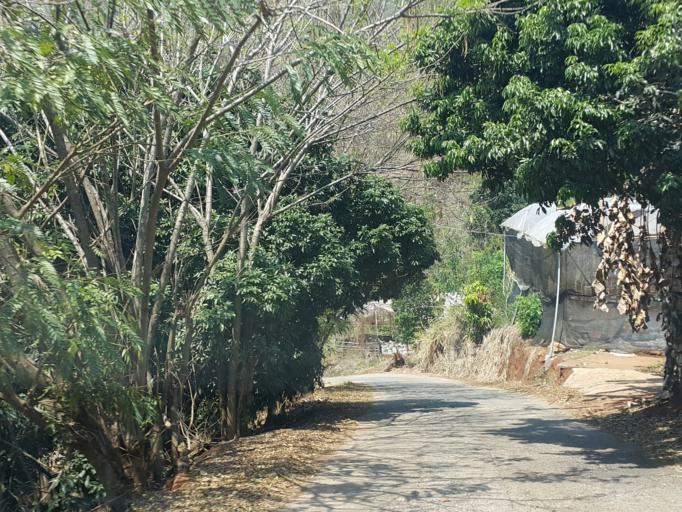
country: TH
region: Chiang Mai
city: Samoeng
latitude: 18.8623
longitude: 98.7842
